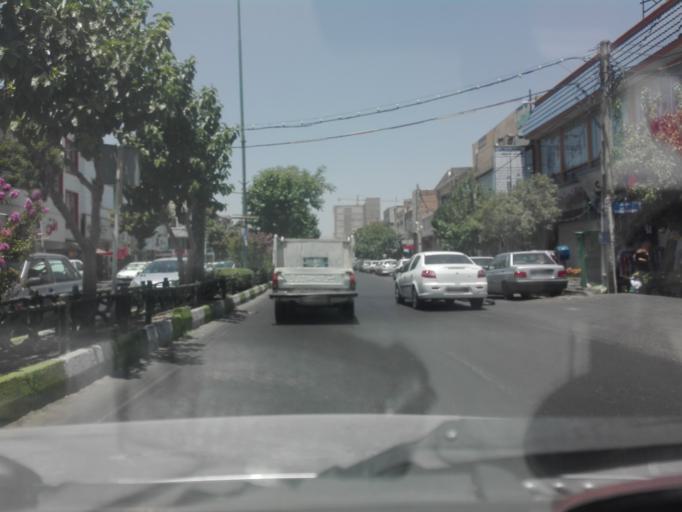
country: IR
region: Tehran
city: Shahre Jadide Andisheh
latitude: 35.7256
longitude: 50.9888
